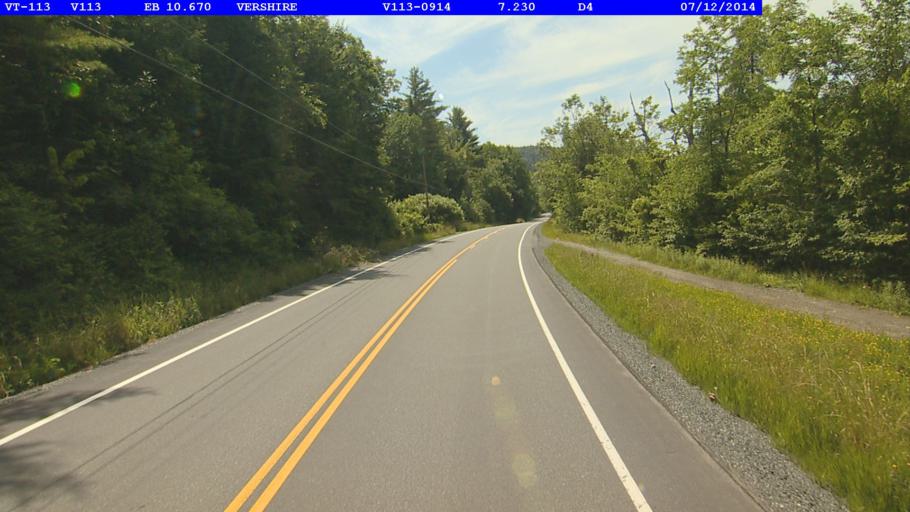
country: US
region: New Hampshire
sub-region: Grafton County
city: Orford
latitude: 43.9431
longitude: -72.2685
